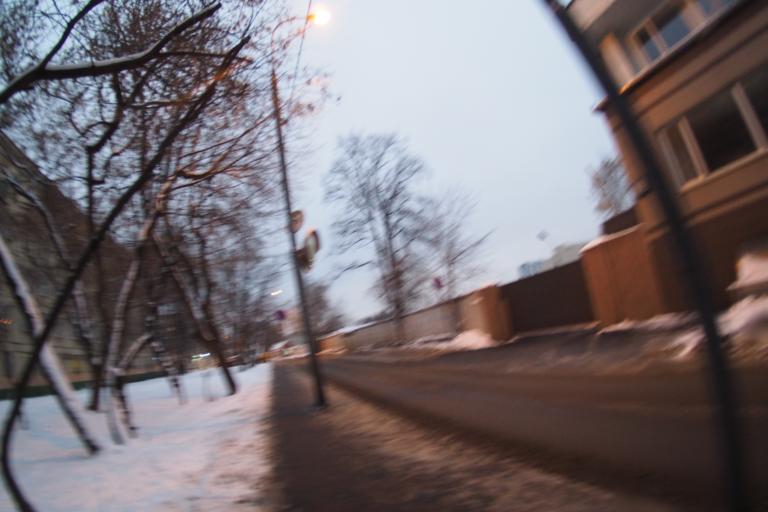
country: RU
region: Moscow
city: Sokol
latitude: 55.8031
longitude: 37.5584
